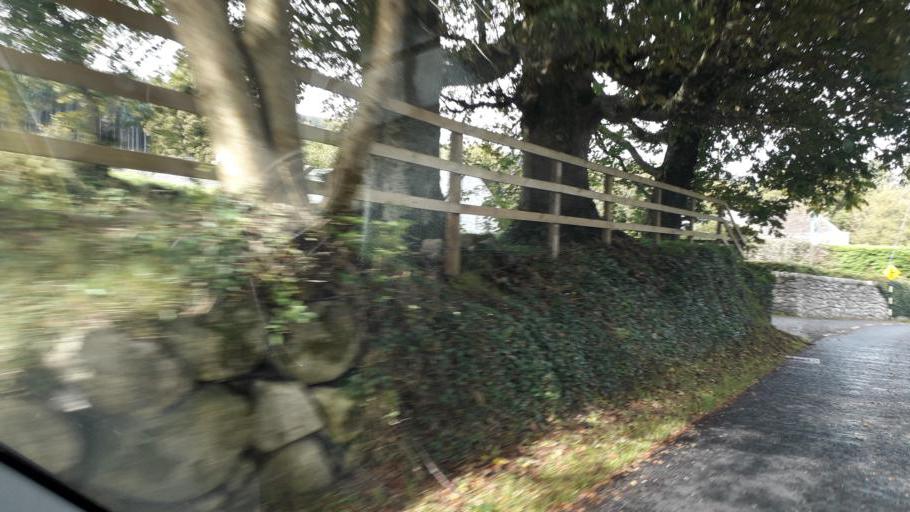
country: IE
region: Leinster
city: Sandyford
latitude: 53.2328
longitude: -6.2218
